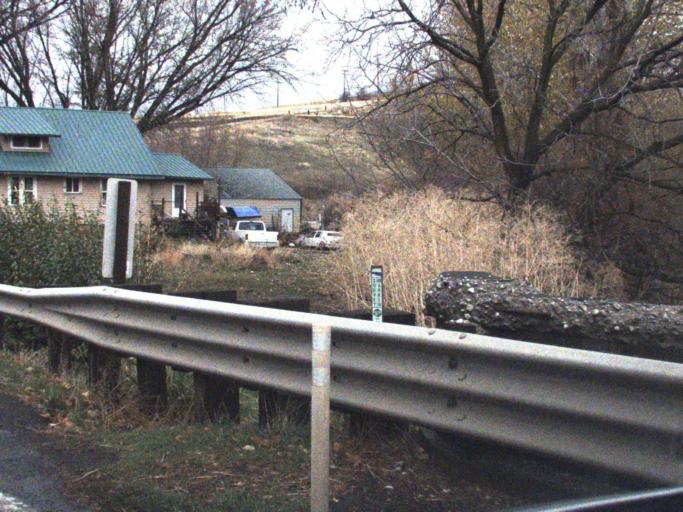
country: US
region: Washington
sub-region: Columbia County
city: Dayton
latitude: 46.3273
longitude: -117.9745
